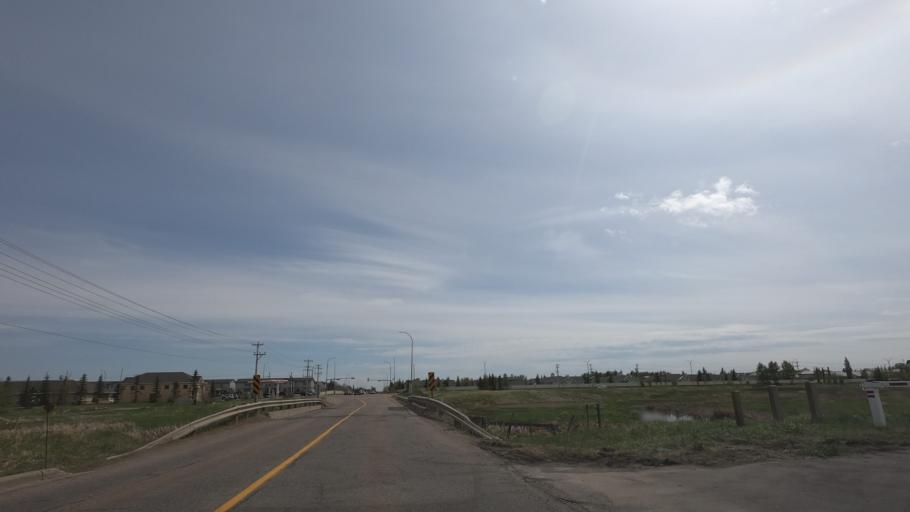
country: CA
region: Alberta
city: Airdrie
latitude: 51.3019
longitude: -114.0254
